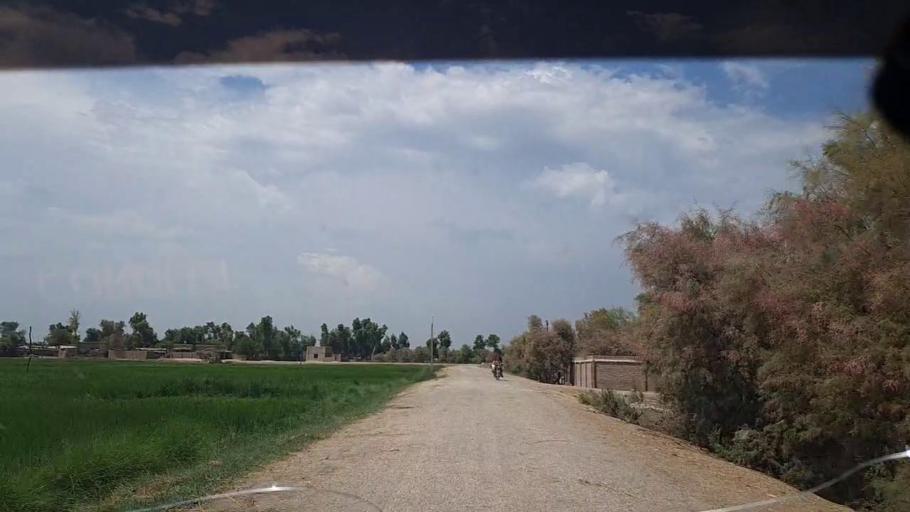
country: PK
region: Sindh
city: Ghauspur
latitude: 28.1534
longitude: 68.9973
